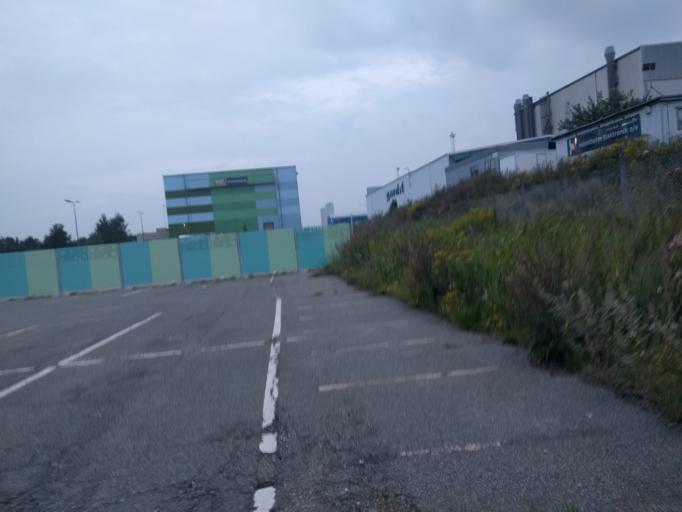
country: DK
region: South Denmark
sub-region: Kerteminde Kommune
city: Munkebo
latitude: 55.4669
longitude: 10.5356
